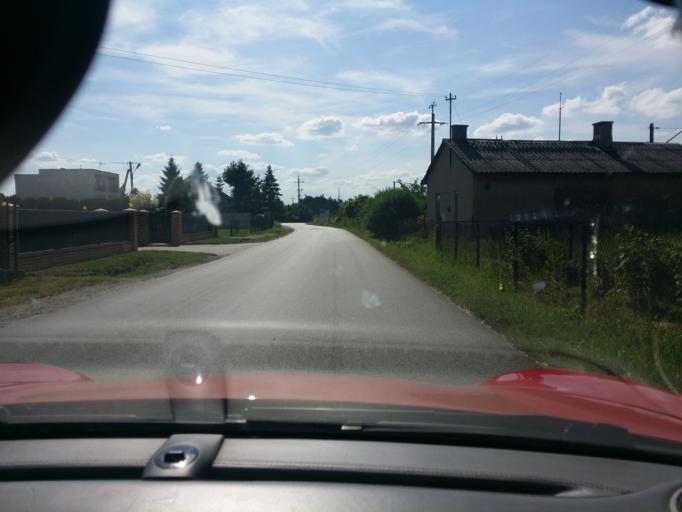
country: PL
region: Masovian Voivodeship
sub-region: Powiat radomski
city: Kowala
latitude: 51.3468
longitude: 21.0876
